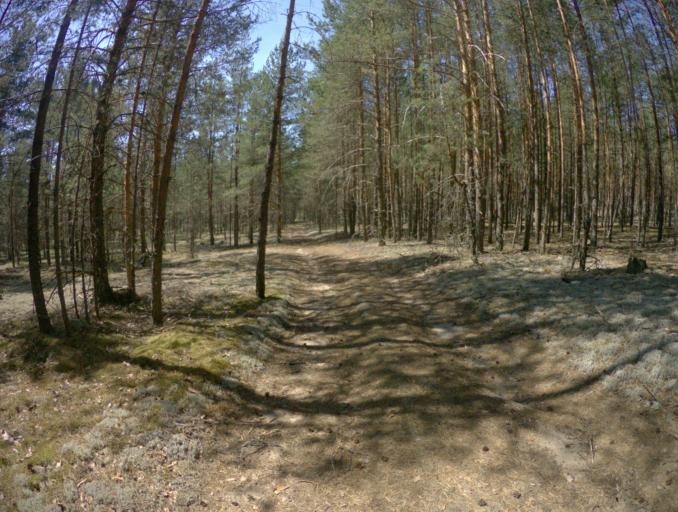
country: RU
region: Ivanovo
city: Talitsy
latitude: 56.3779
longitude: 42.3049
